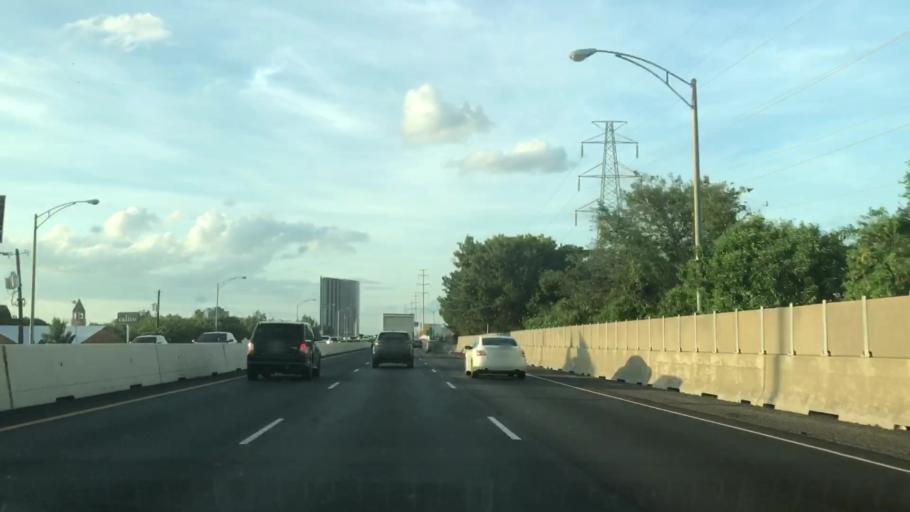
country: US
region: Texas
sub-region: Dallas County
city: Addison
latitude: 32.9166
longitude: -96.8170
